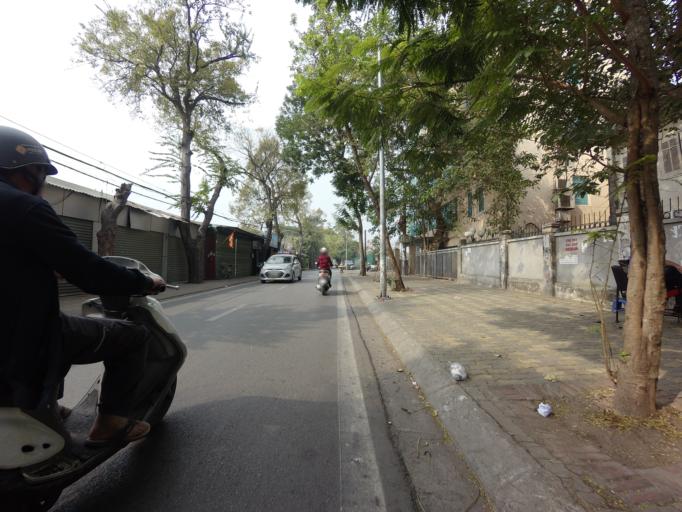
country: VN
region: Ha Noi
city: Tay Ho
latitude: 21.0560
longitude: 105.8349
